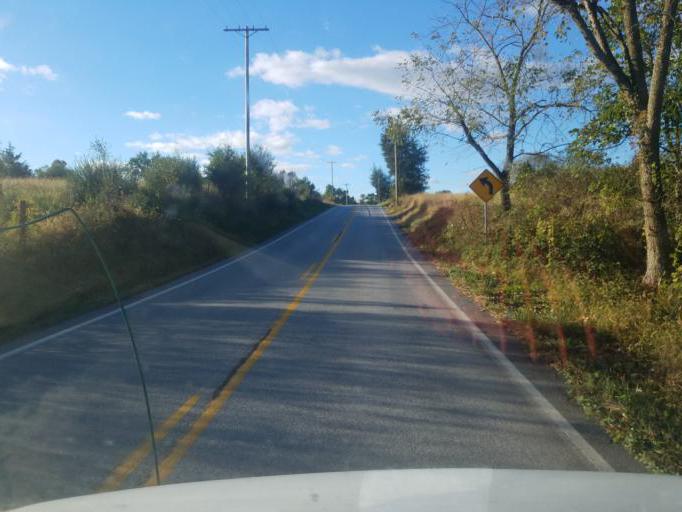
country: US
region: Pennsylvania
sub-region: Adams County
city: Gettysburg
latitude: 39.8757
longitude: -77.2306
